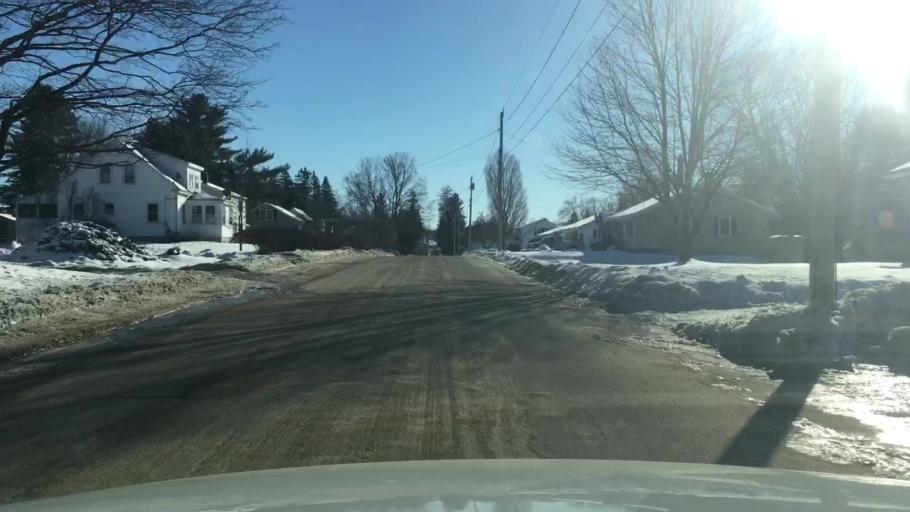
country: US
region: Maine
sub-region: Kennebec County
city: Winthrop
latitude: 44.3104
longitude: -69.9695
